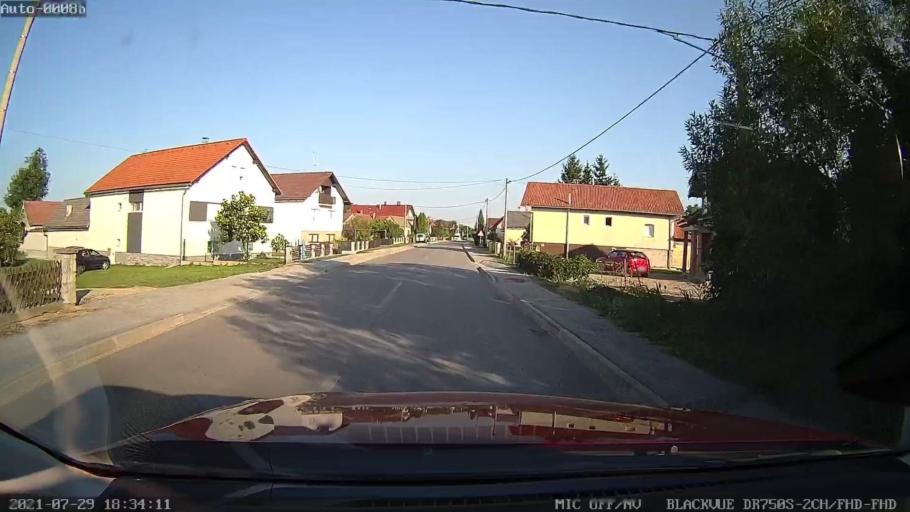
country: HR
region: Varazdinska
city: Vinica
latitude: 46.3114
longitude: 16.1640
